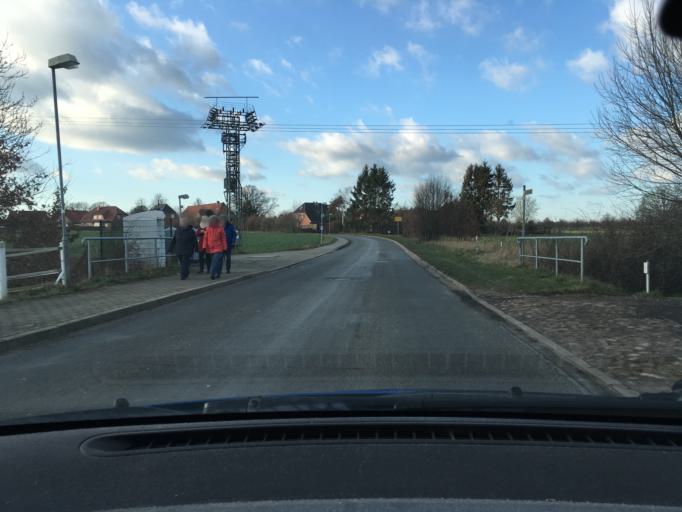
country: DE
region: Schleswig-Holstein
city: Schulendorf
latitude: 53.4725
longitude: 10.5666
